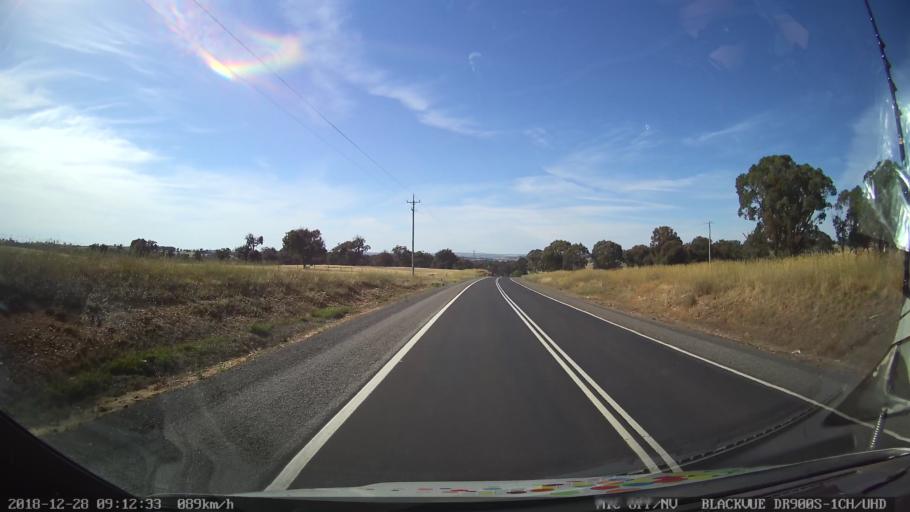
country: AU
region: New South Wales
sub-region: Upper Lachlan Shire
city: Crookwell
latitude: -34.2570
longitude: 149.3422
